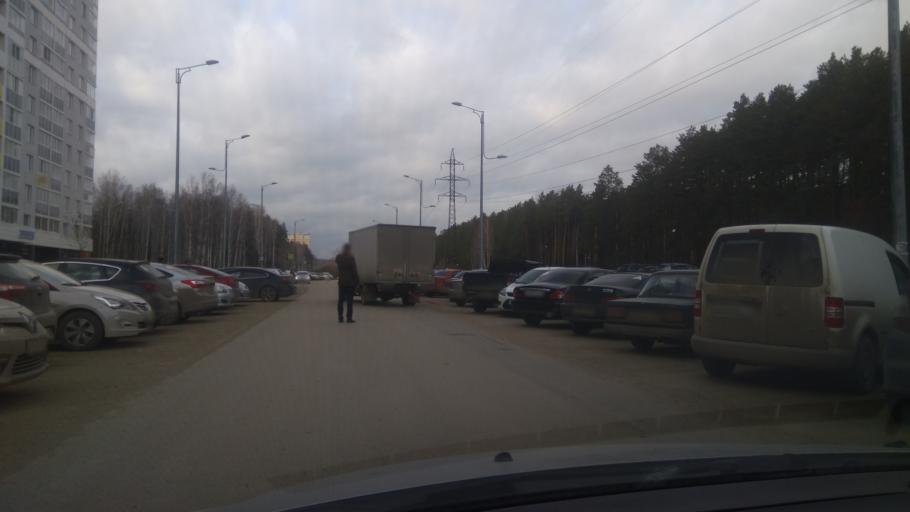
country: RU
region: Sverdlovsk
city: Sovkhoznyy
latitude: 56.7862
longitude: 60.5485
